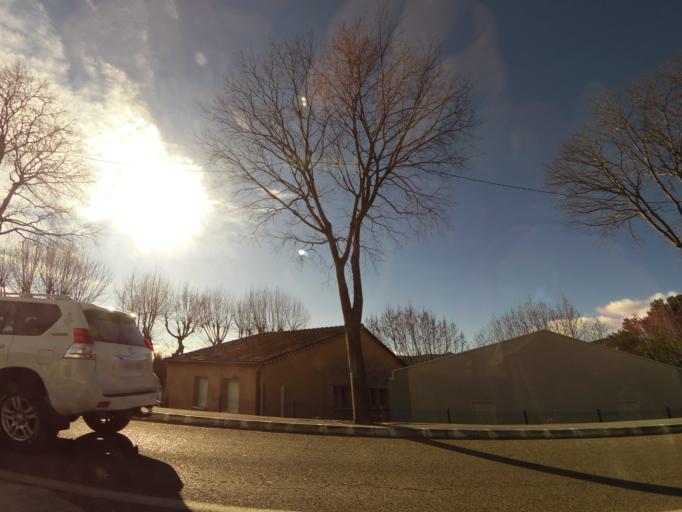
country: FR
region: Languedoc-Roussillon
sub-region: Departement du Gard
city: Quissac
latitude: 43.9079
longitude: 4.0034
